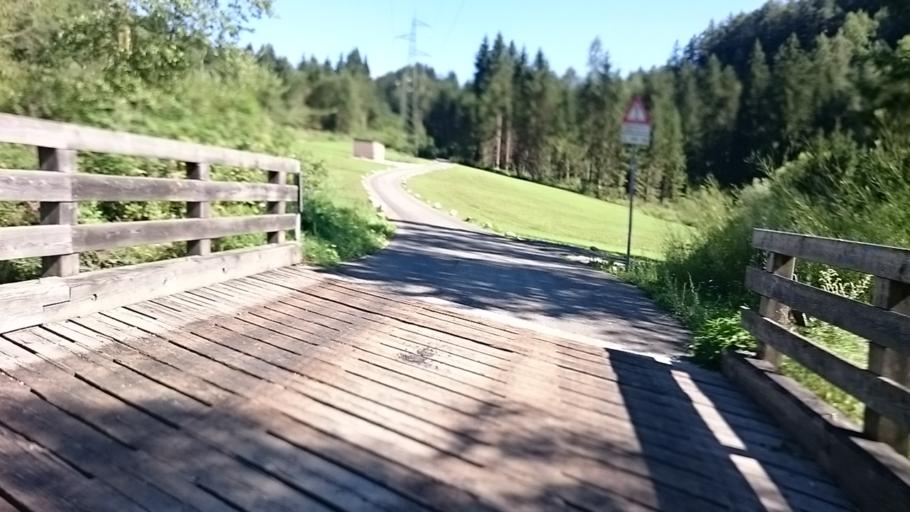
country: IT
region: Trentino-Alto Adige
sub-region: Bolzano
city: Perca
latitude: 46.7881
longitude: 11.9937
